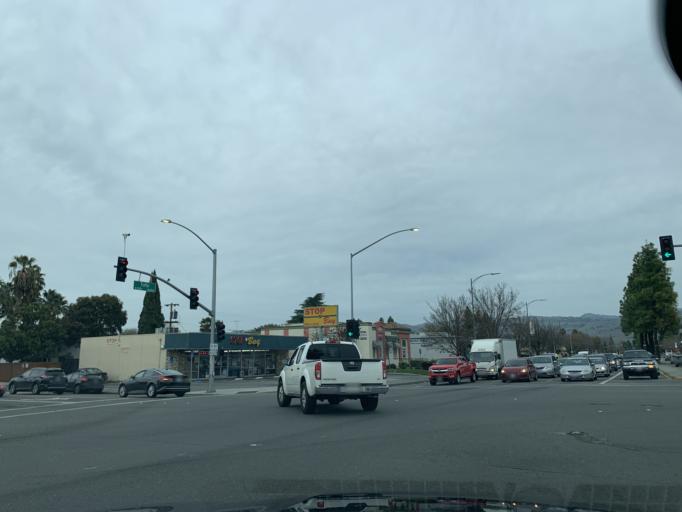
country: US
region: California
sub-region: Santa Clara County
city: Seven Trees
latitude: 37.3202
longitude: -121.8291
